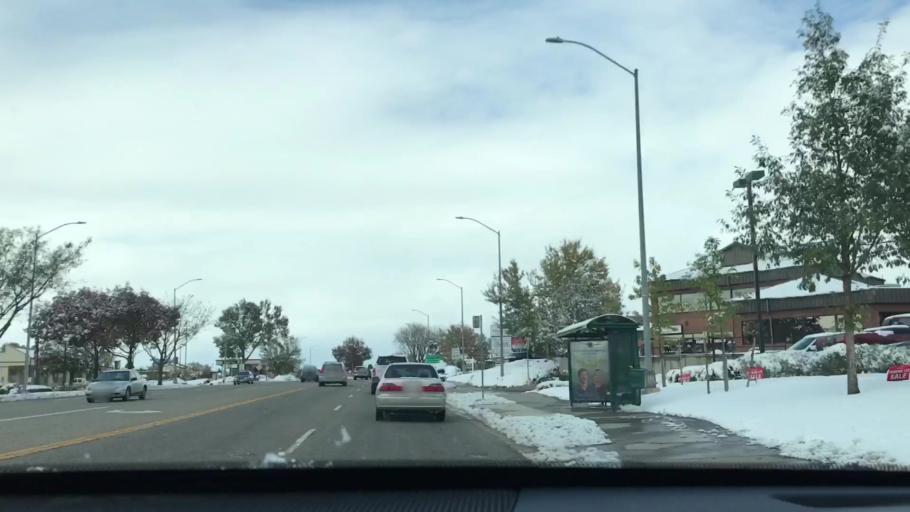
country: US
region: Colorado
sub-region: Boulder County
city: Longmont
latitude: 40.1997
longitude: -105.1024
